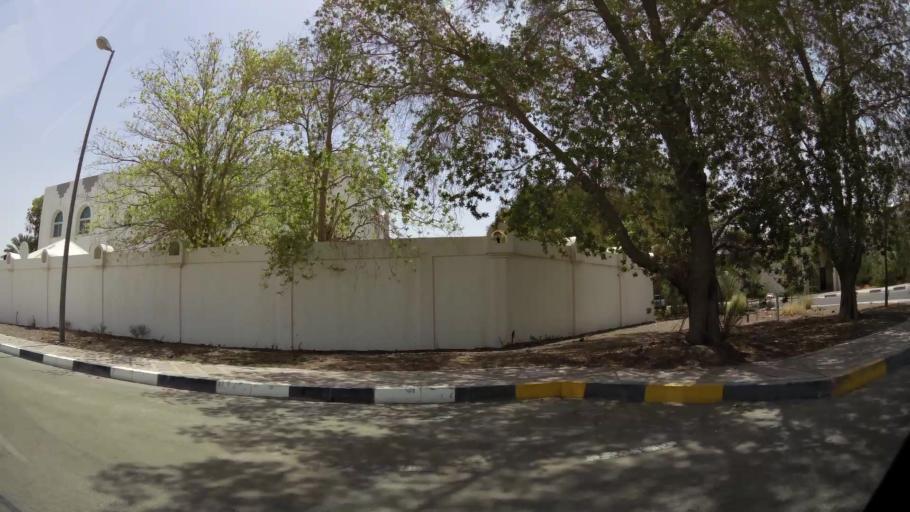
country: AE
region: Abu Dhabi
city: Al Ain
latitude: 24.1975
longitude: 55.7380
